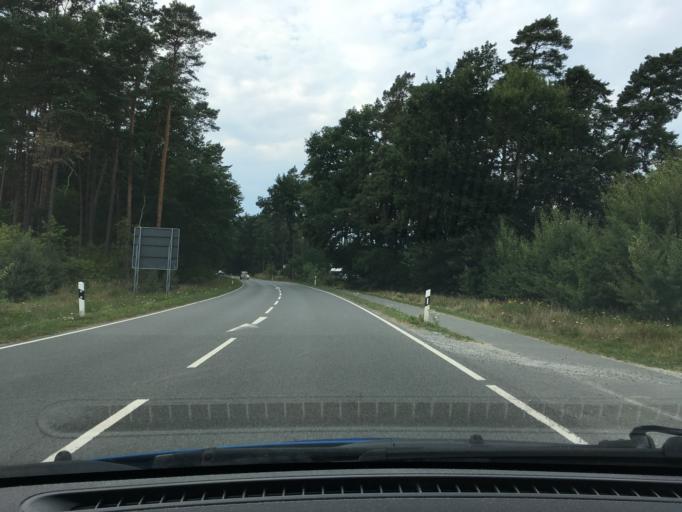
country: DE
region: Lower Saxony
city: Adelheidsdorf
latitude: 52.5618
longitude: 10.0688
